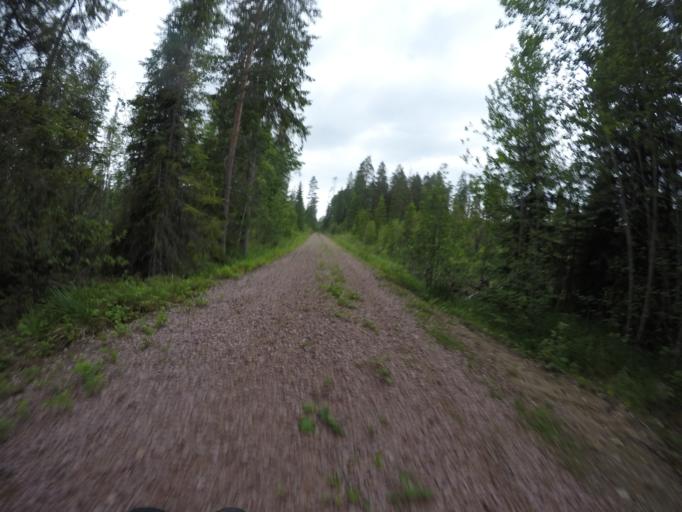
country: SE
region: OErebro
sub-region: Hallefors Kommun
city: Haellefors
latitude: 60.0230
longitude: 14.5758
